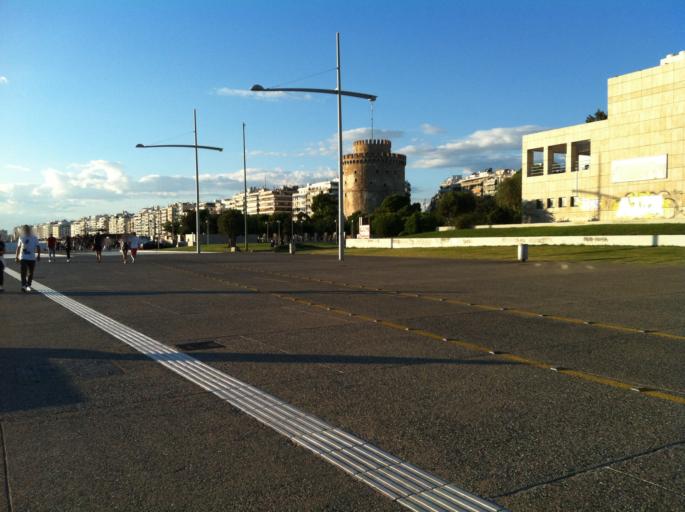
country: GR
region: Central Macedonia
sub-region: Nomos Thessalonikis
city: Agios Pavlos
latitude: 40.6245
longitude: 22.9490
